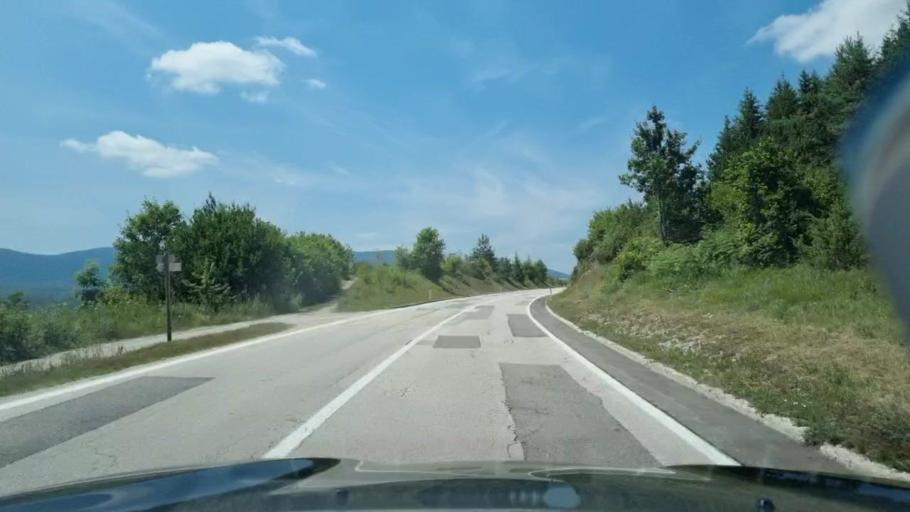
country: BA
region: Federation of Bosnia and Herzegovina
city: Sanica
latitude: 44.5453
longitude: 16.6281
